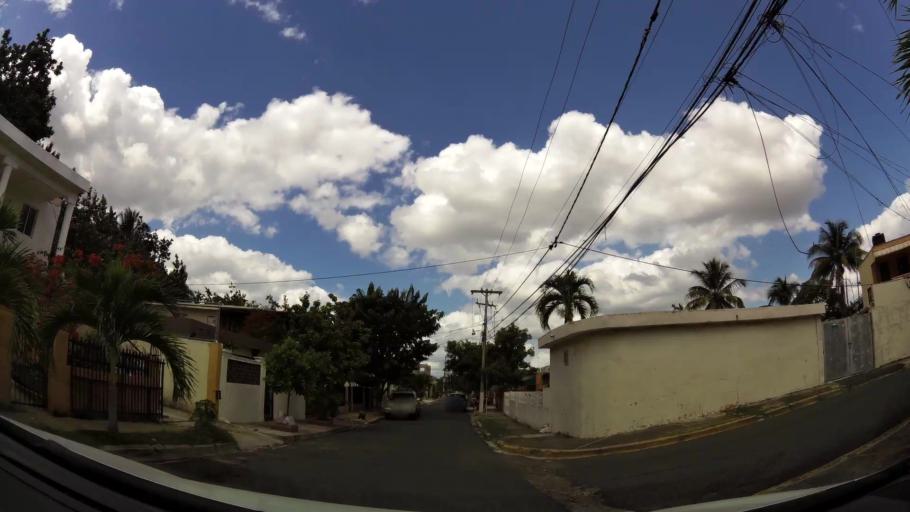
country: DO
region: Nacional
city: Ensanche Luperon
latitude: 18.5170
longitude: -69.9098
